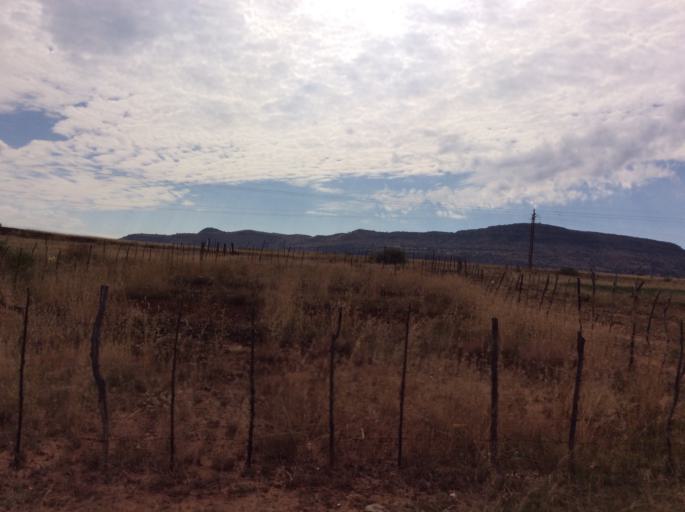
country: LS
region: Mafeteng
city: Mafeteng
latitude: -29.7205
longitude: 27.0088
